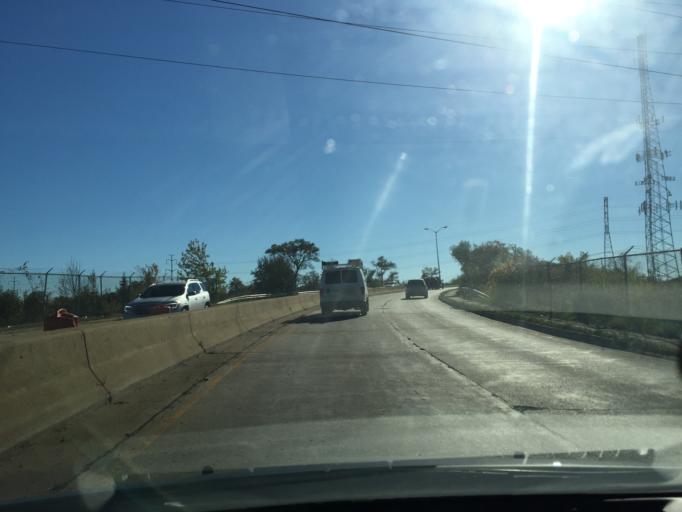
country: US
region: Michigan
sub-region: Oakland County
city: Pontiac
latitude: 42.6188
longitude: -83.2684
